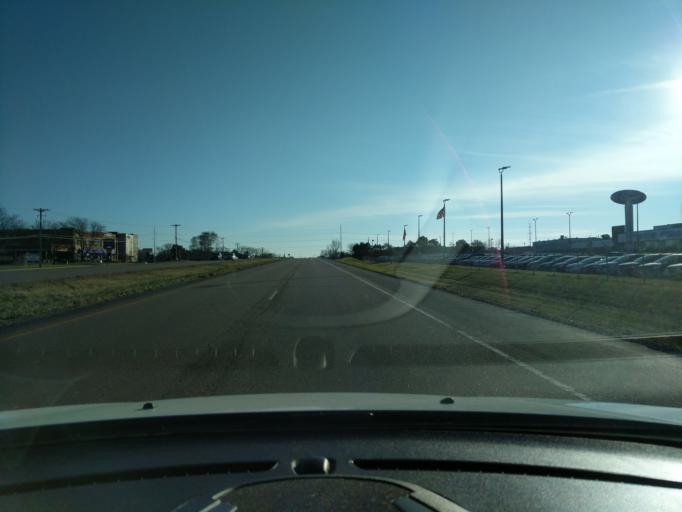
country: US
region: Minnesota
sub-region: Ramsey County
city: Roseville
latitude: 45.0256
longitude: -93.1672
